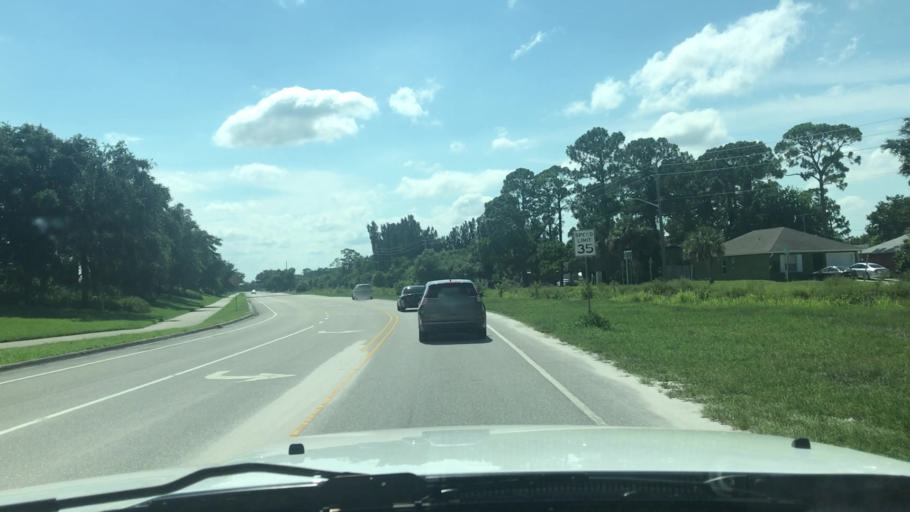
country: US
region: Florida
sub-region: Indian River County
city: Florida Ridge
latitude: 27.5721
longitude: -80.4065
